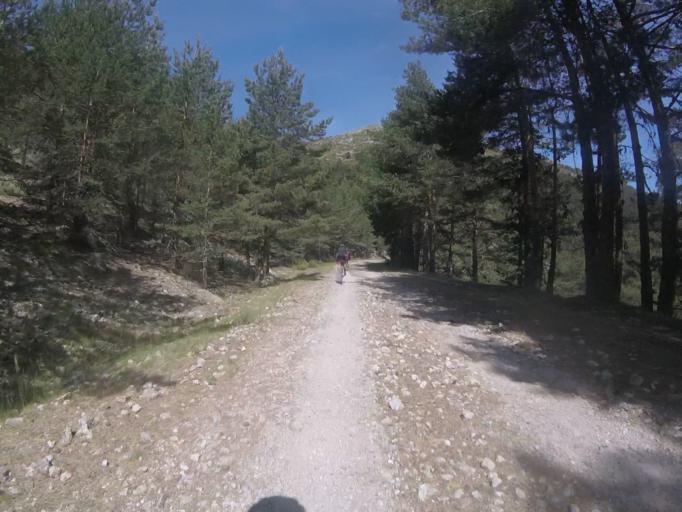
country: ES
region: Madrid
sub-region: Provincia de Madrid
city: Cercedilla
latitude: 40.7950
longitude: -4.0629
